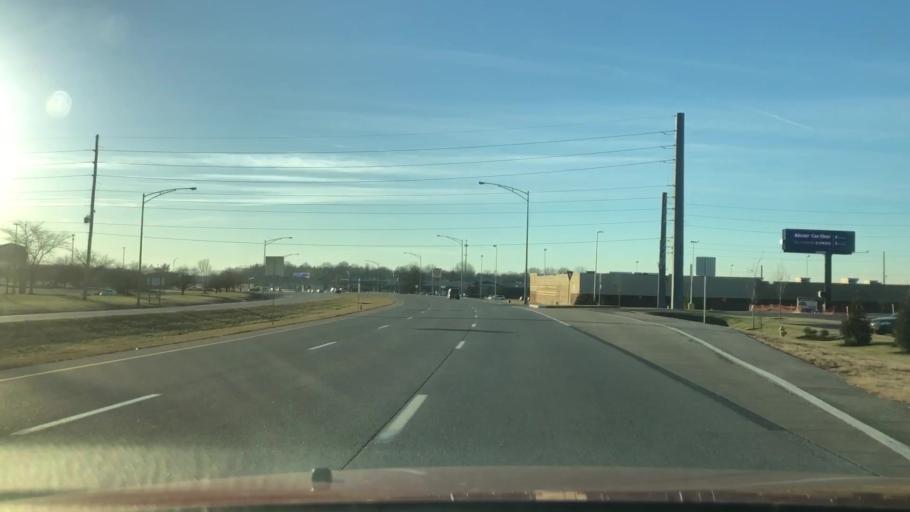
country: US
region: Missouri
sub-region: Greene County
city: Springfield
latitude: 37.1537
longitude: -93.2627
